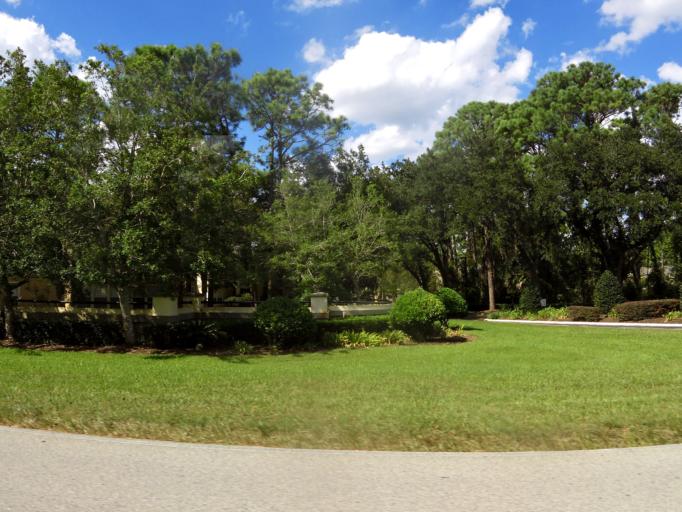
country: US
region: Florida
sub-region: Saint Johns County
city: Ponte Vedra Beach
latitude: 30.2492
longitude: -81.3934
